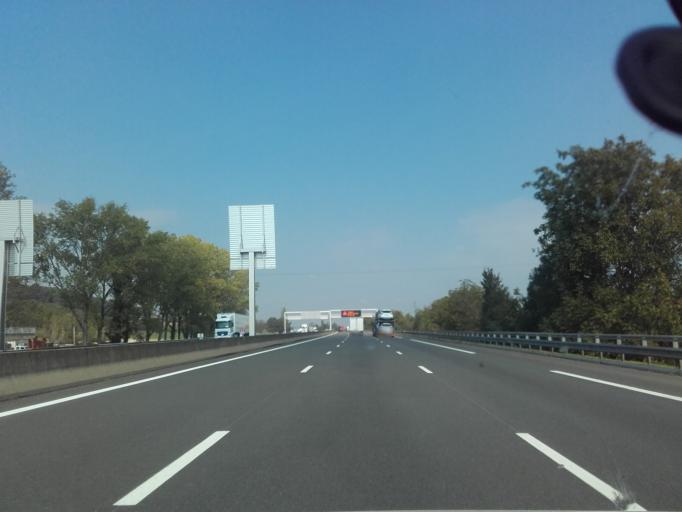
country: FR
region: Bourgogne
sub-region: Departement de Saone-et-Loire
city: Saint-Martin-Belle-Roche
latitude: 46.3849
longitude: 4.8500
